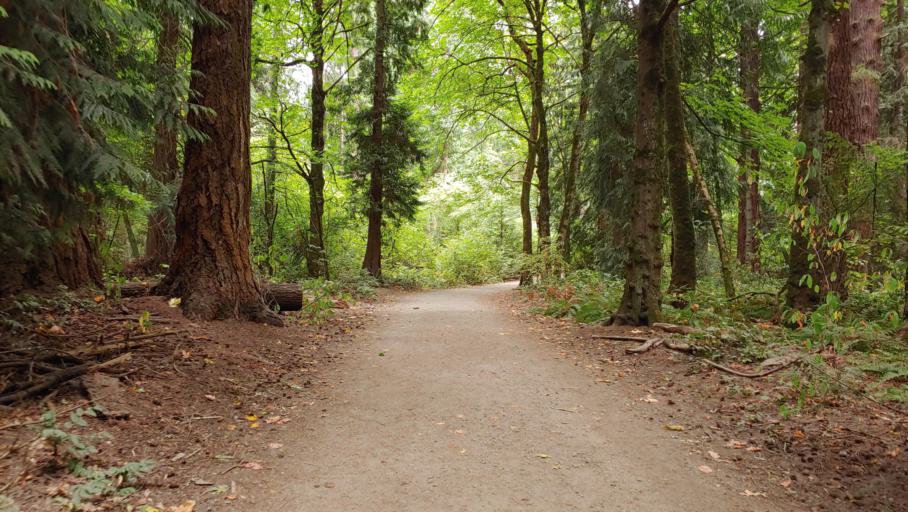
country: US
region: Washington
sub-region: King County
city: Mercer Island
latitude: 47.5551
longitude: -122.2504
